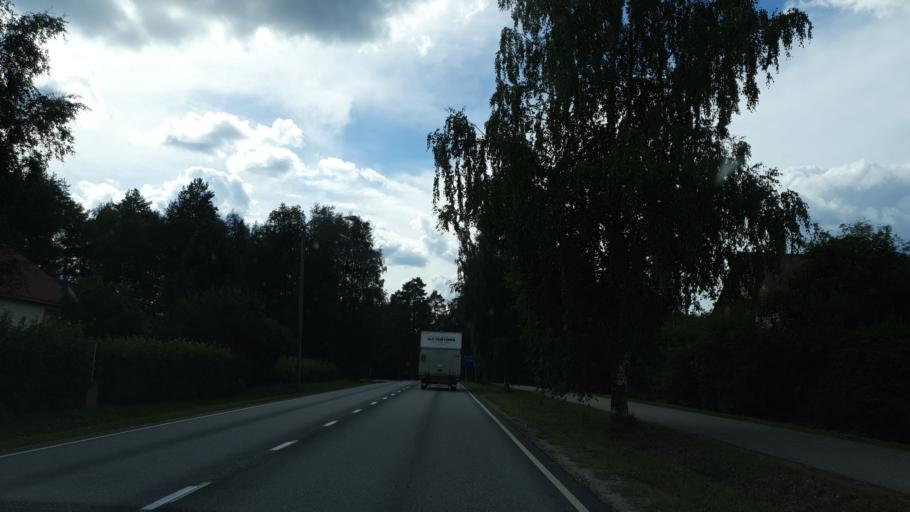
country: FI
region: Kainuu
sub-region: Kajaani
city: Sotkamo
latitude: 64.1330
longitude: 28.4056
